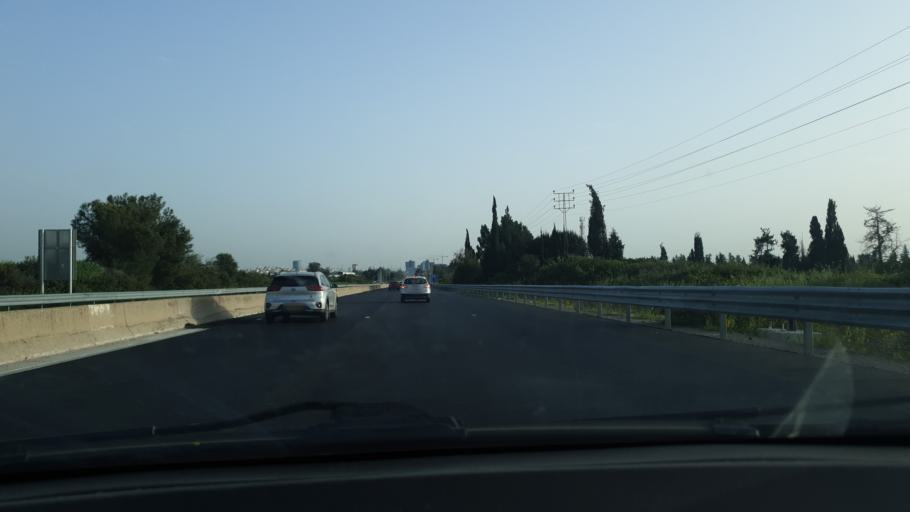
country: IL
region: Central District
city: Ra'anana
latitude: 32.2243
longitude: 34.8828
